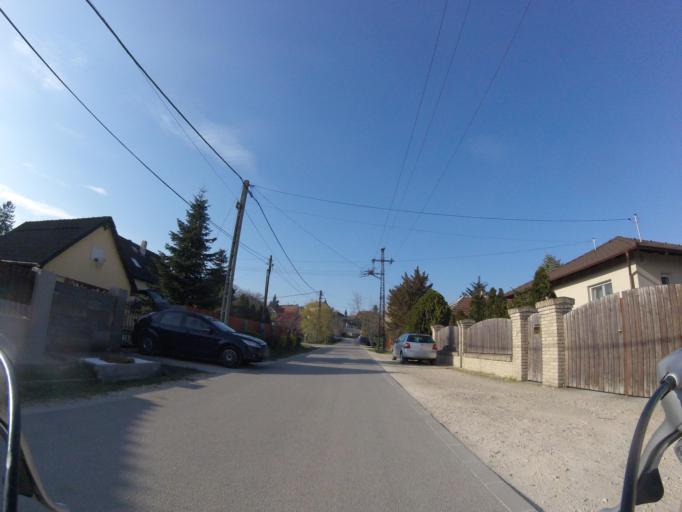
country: HU
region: Pest
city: Diosd
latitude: 47.3875
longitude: 18.9416
